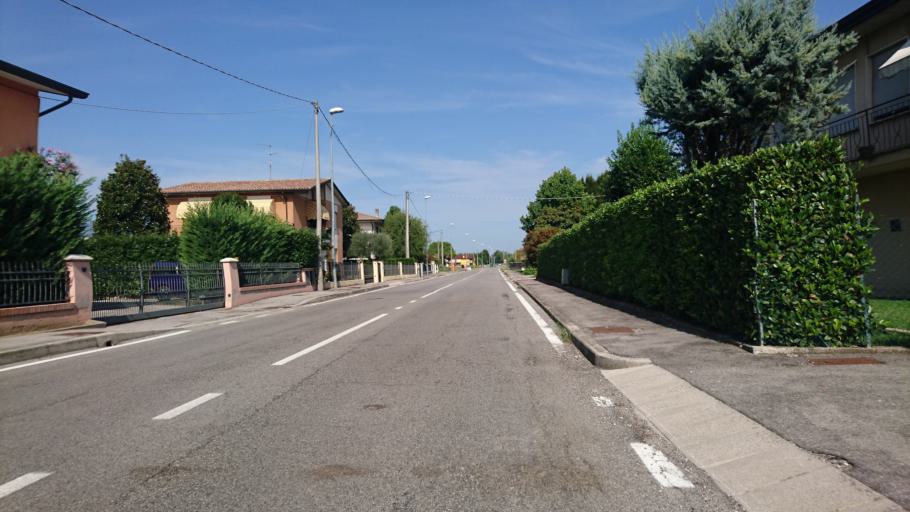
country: IT
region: Veneto
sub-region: Provincia di Padova
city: Veggiano
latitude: 45.4393
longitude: 11.6995
